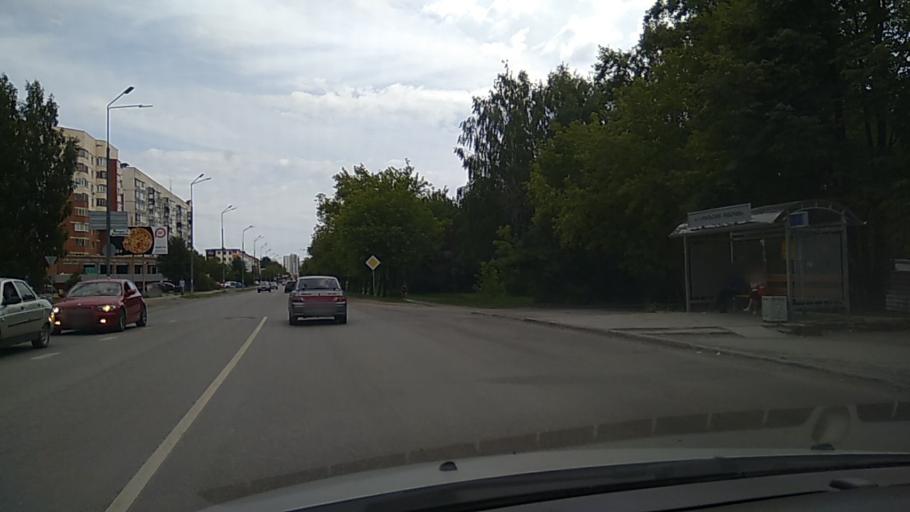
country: RU
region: Sverdlovsk
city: Verkhnyaya Pyshma
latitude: 56.9795
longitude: 60.5530
